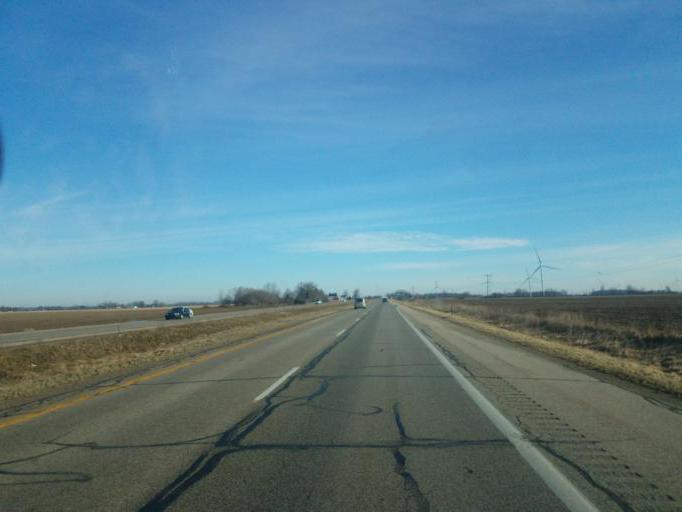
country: US
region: Michigan
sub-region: Gratiot County
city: Ithaca
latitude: 43.2583
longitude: -84.5631
